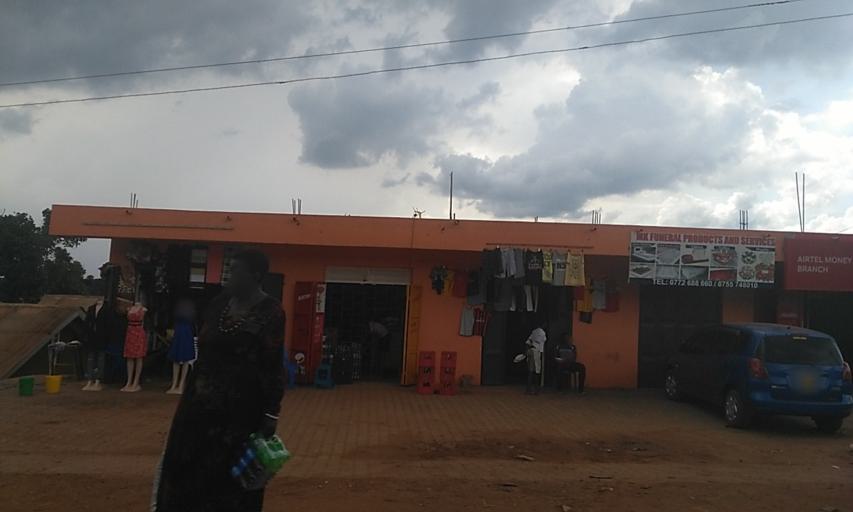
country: UG
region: Central Region
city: Kampala Central Division
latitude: 0.3304
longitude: 32.4962
